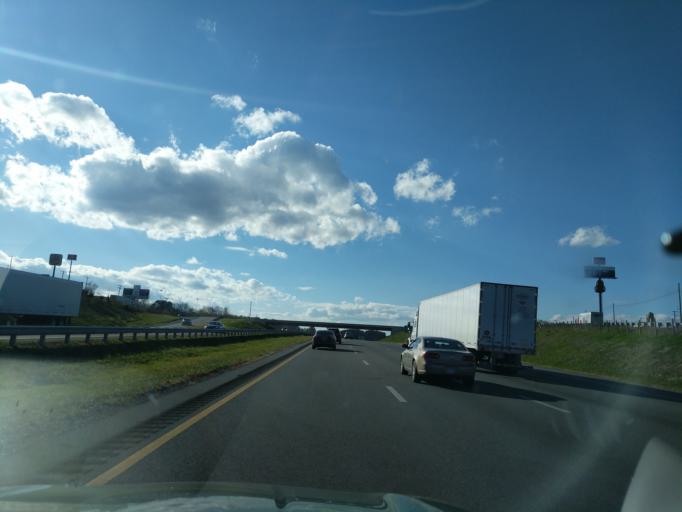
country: US
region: Virginia
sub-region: Wythe County
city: Wytheville
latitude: 36.9371
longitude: -80.9894
